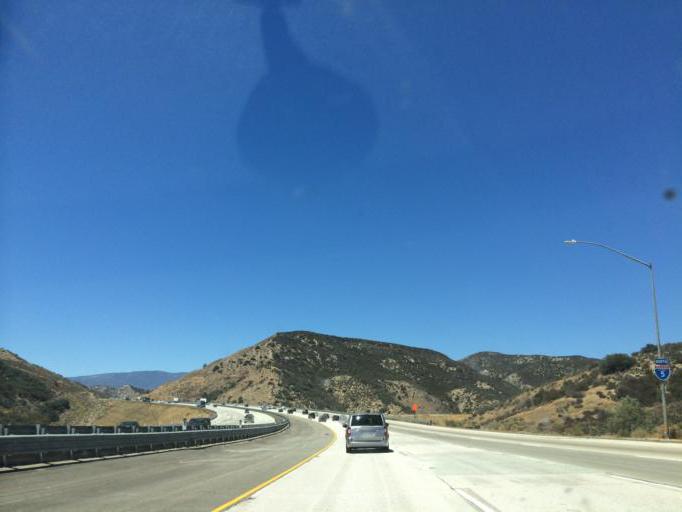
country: US
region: California
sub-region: Kern County
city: Lebec
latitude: 34.6701
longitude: -118.7652
